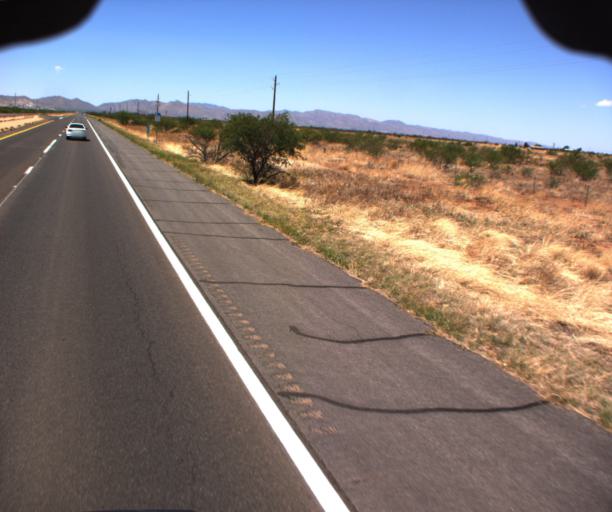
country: US
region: Arizona
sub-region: Cochise County
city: Pirtleville
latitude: 31.3601
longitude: -109.6571
